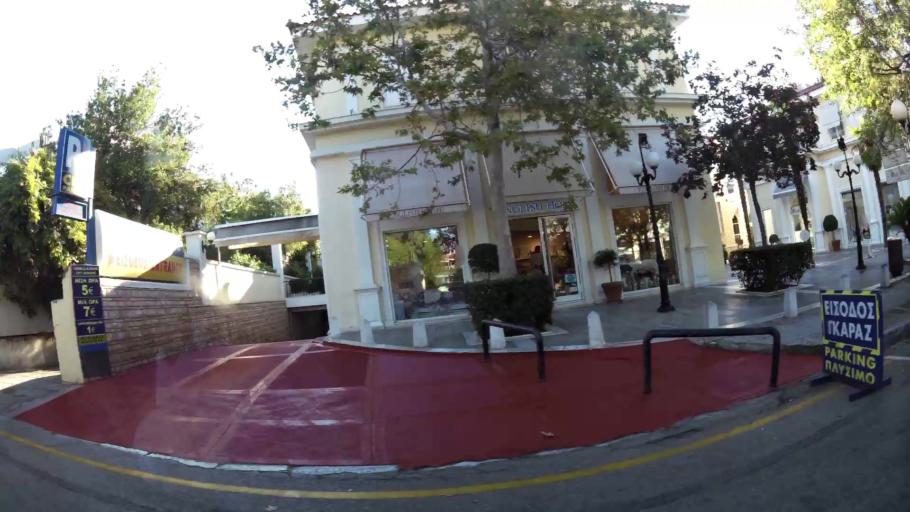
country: GR
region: Attica
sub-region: Nomarchia Athinas
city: Kifisia
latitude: 38.0738
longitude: 23.8148
